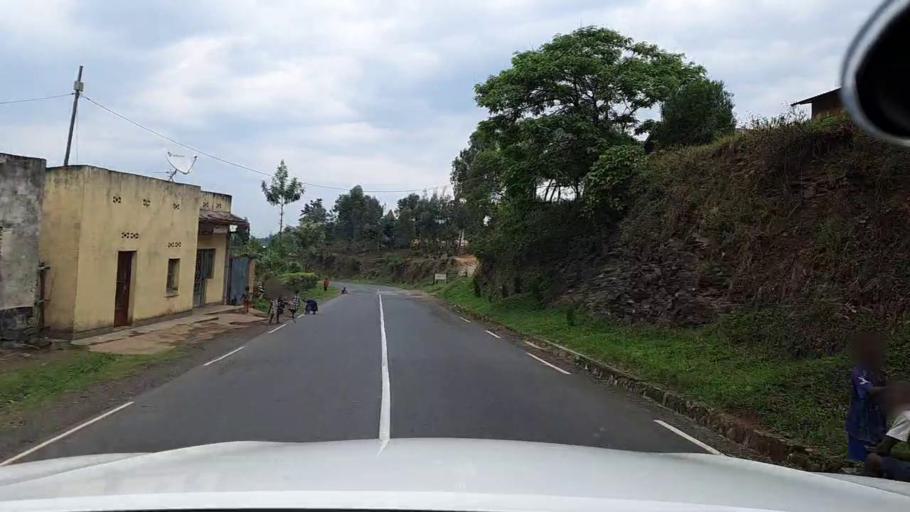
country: RW
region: Western Province
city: Cyangugu
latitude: -2.6593
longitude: 28.9787
